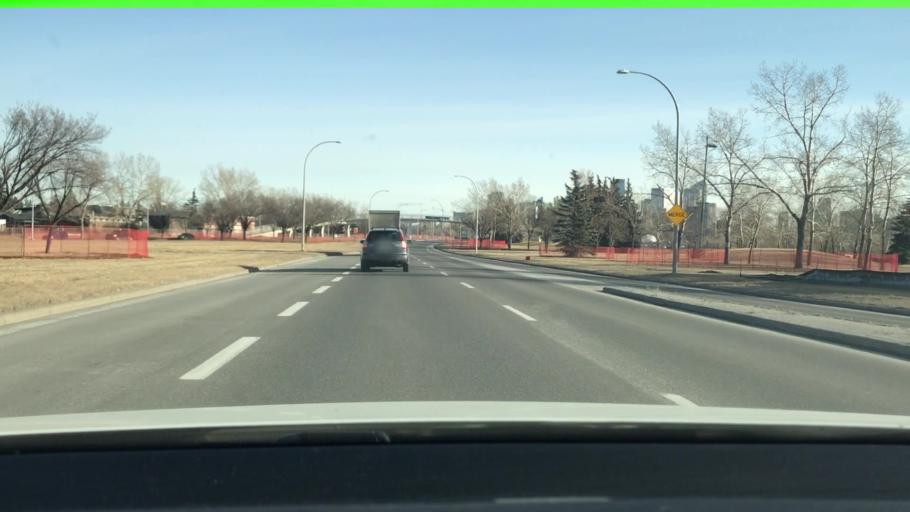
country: CA
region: Alberta
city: Calgary
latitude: 51.0487
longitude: -114.1133
